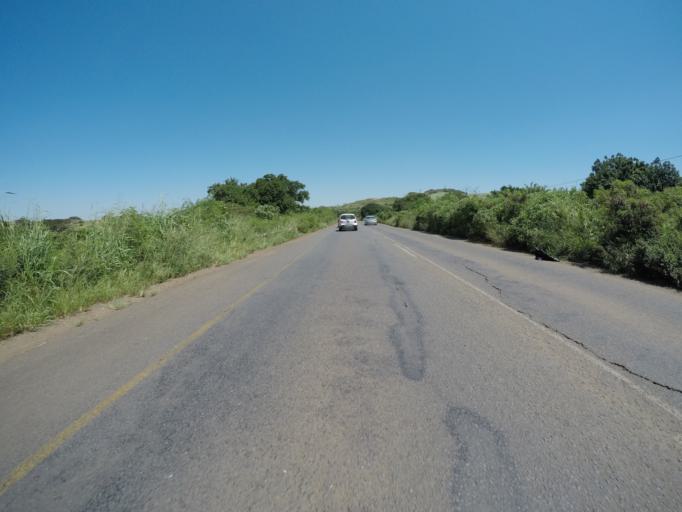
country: ZA
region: KwaZulu-Natal
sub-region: uThungulu District Municipality
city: Empangeni
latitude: -28.7504
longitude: 31.8786
